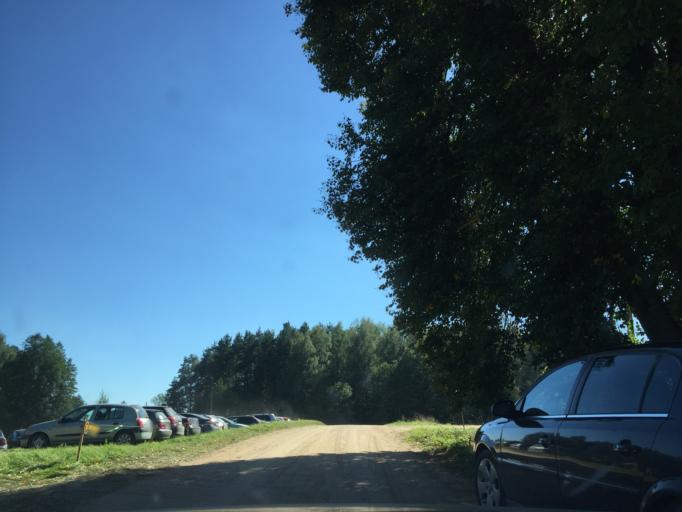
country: LT
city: Zarasai
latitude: 55.7881
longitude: 25.9537
